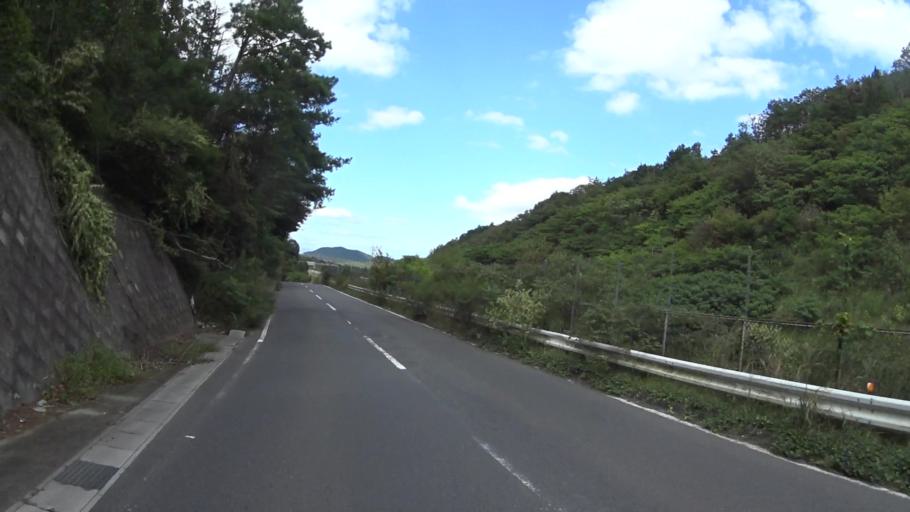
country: JP
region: Shiga Prefecture
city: Otsu-shi
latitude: 34.9308
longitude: 135.8884
